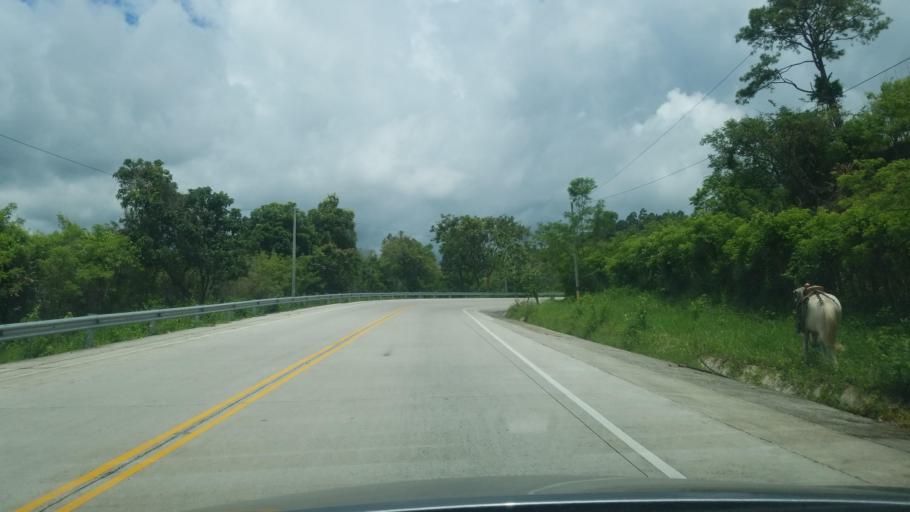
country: HN
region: Copan
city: San Jeronimo
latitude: 14.9949
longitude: -88.8469
